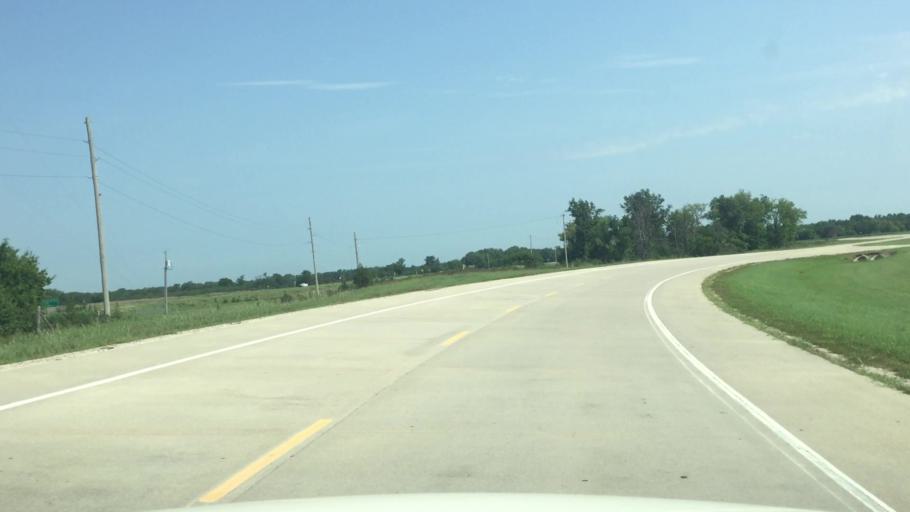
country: US
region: Kansas
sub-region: Montgomery County
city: Coffeyville
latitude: 37.1038
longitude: -95.5861
